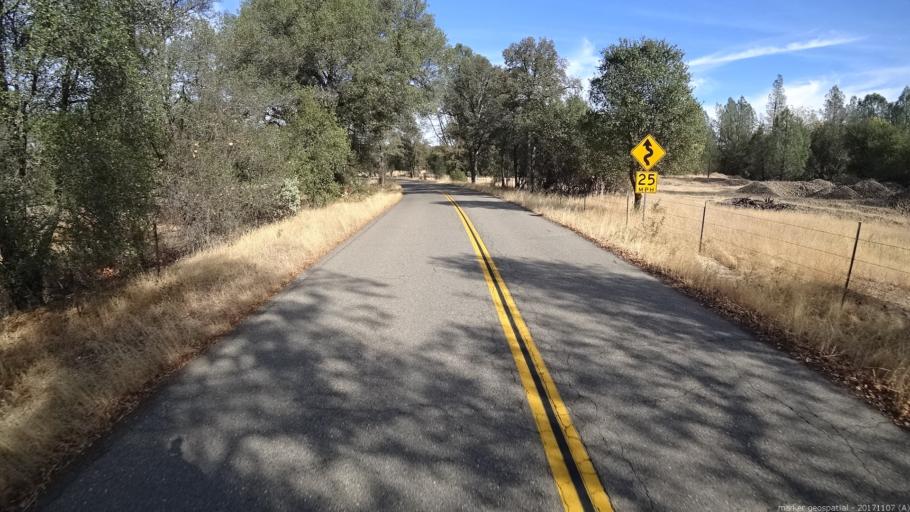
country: US
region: California
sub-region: Shasta County
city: Shasta
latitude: 40.4017
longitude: -122.5201
